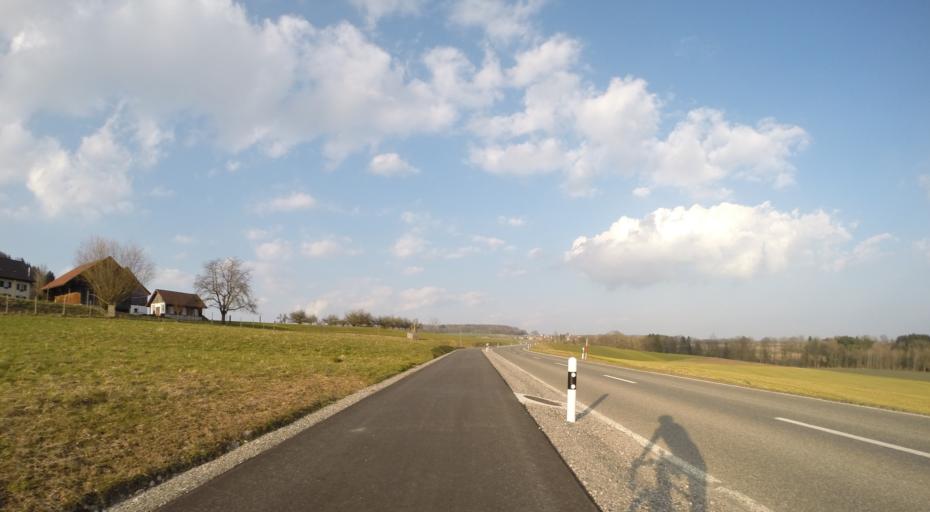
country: CH
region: Thurgau
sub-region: Frauenfeld District
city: Pfyn
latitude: 47.6158
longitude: 8.9203
